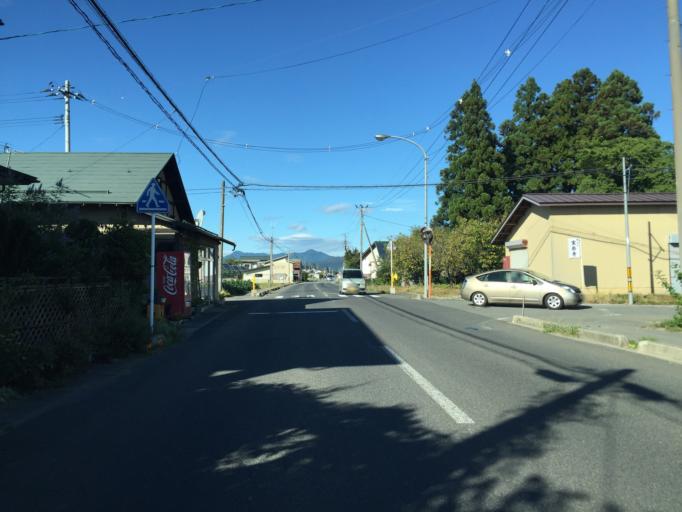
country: JP
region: Yamagata
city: Takahata
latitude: 37.9697
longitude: 140.1600
